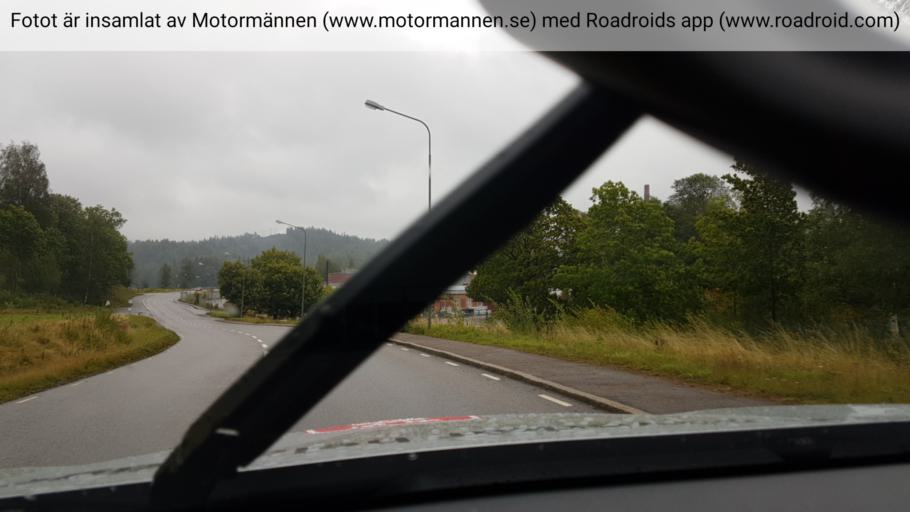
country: SE
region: Vaestra Goetaland
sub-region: Bengtsfors Kommun
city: Billingsfors
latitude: 58.9855
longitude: 12.2516
